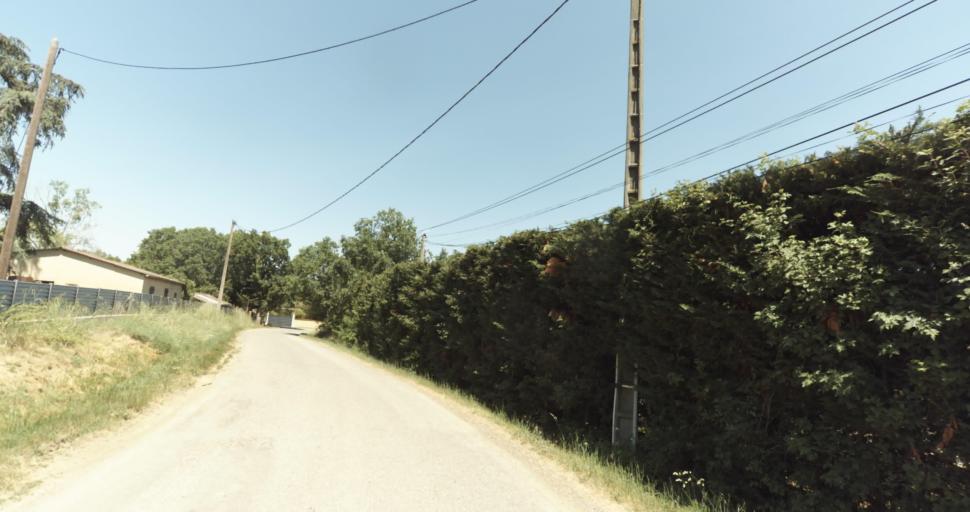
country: FR
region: Midi-Pyrenees
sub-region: Departement de la Haute-Garonne
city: Levignac
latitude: 43.6346
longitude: 1.1816
